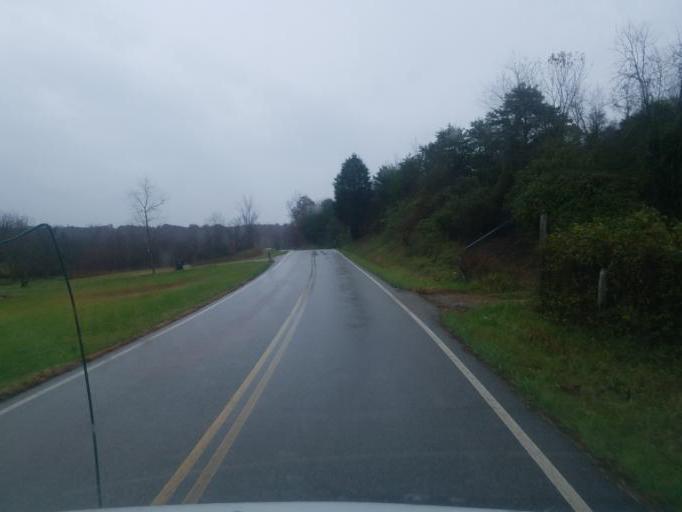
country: US
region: West Virginia
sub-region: Wood County
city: Blennerhassett
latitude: 39.3296
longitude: -81.6210
